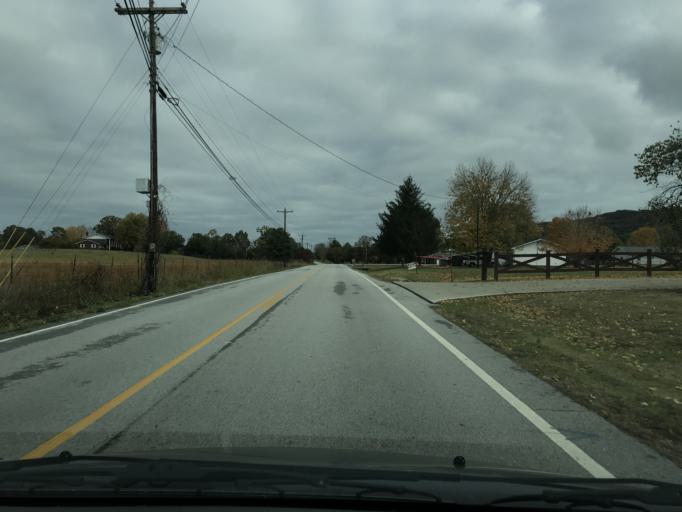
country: US
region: Tennessee
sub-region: Hamilton County
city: Lakesite
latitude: 35.1837
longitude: -85.0239
